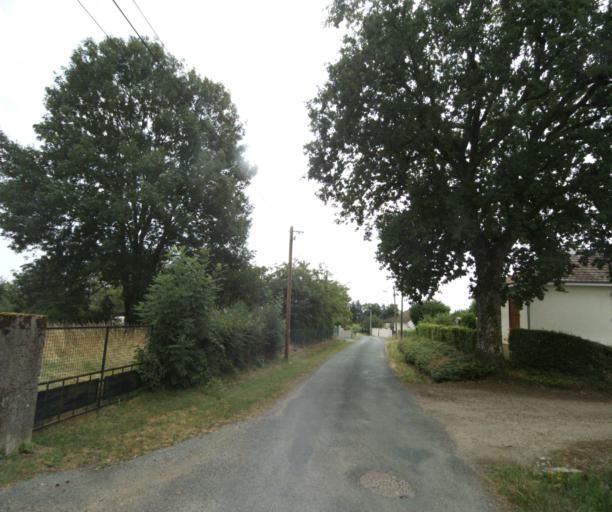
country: FR
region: Bourgogne
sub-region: Departement de Saone-et-Loire
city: Gueugnon
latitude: 46.5947
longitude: 4.0411
